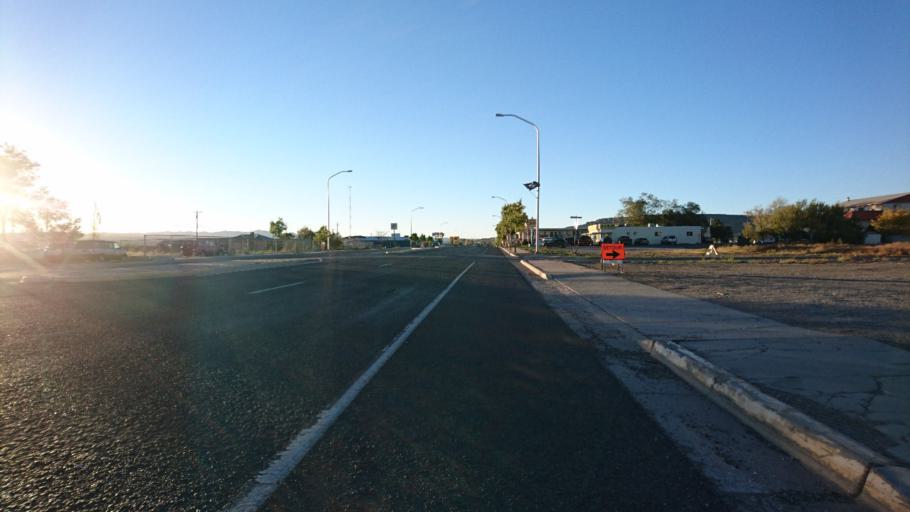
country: US
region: New Mexico
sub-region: Cibola County
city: Grants
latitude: 35.1409
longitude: -107.8308
